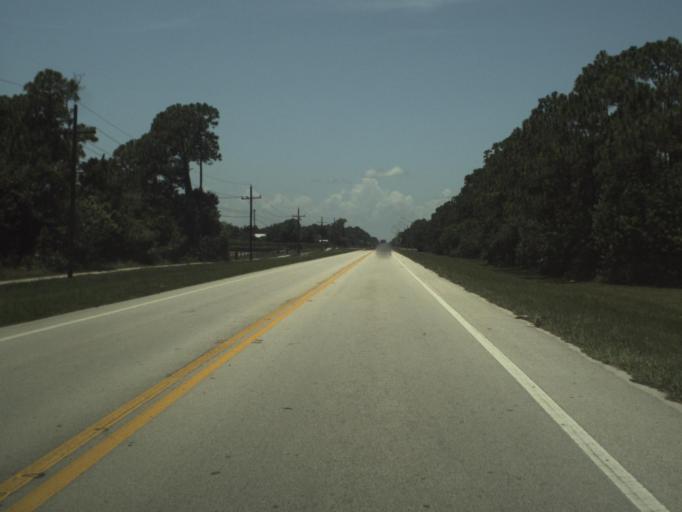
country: US
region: Florida
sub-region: Martin County
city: Palm City
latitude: 27.1616
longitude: -80.3295
